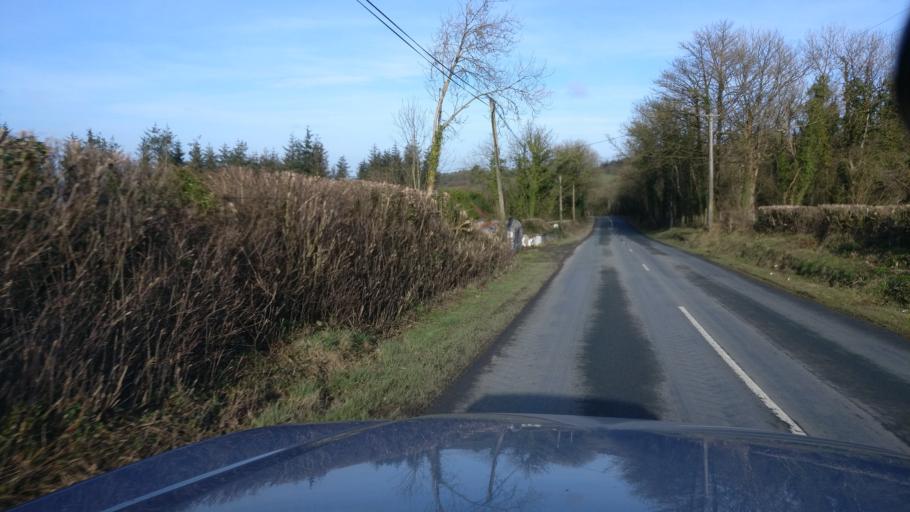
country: IE
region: Leinster
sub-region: Laois
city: Stradbally
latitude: 52.9341
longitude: -7.1976
